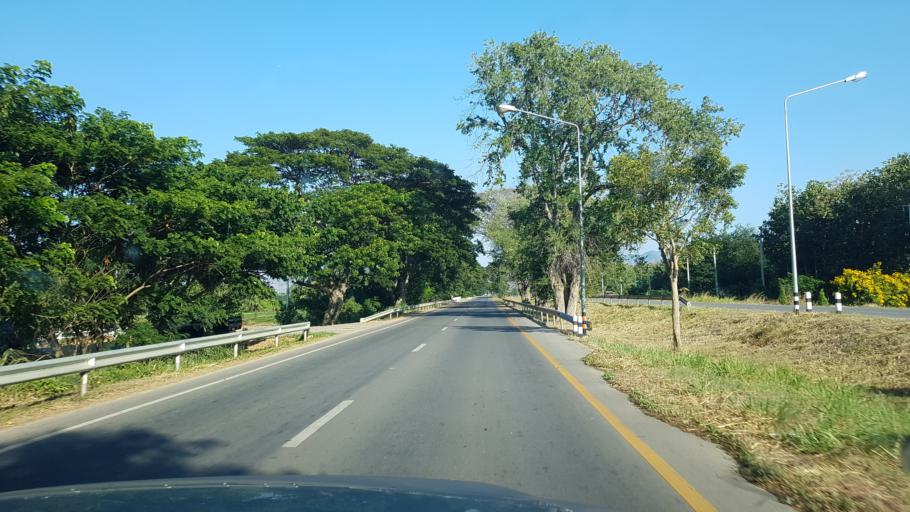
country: TH
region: Phetchabun
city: Lom Sak
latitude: 16.7267
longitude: 101.2488
